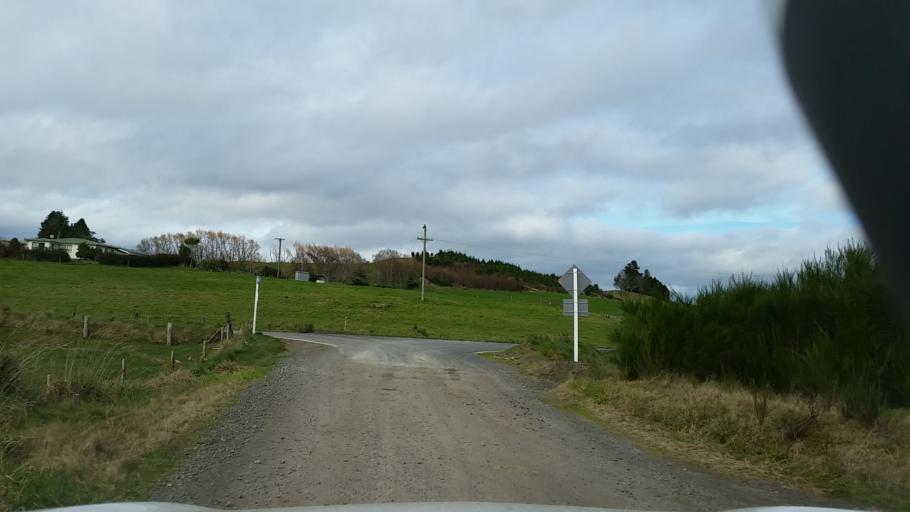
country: NZ
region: Bay of Plenty
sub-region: Whakatane District
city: Murupara
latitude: -38.2918
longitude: 176.5449
